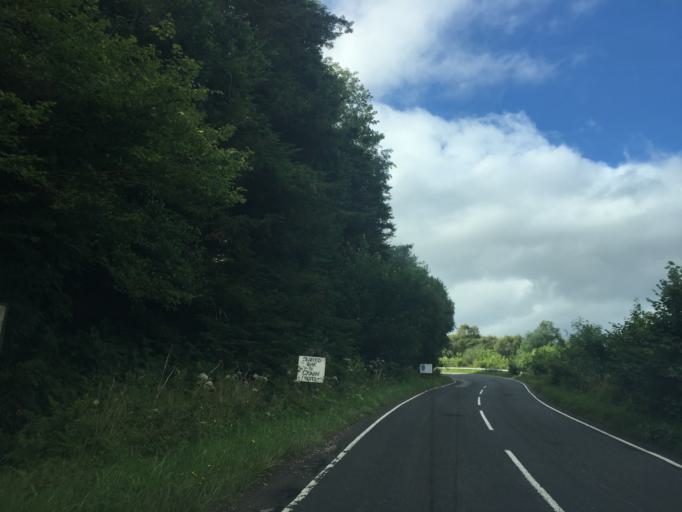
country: GB
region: Scotland
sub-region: Argyll and Bute
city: Ardrishaig
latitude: 56.0746
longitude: -5.5344
